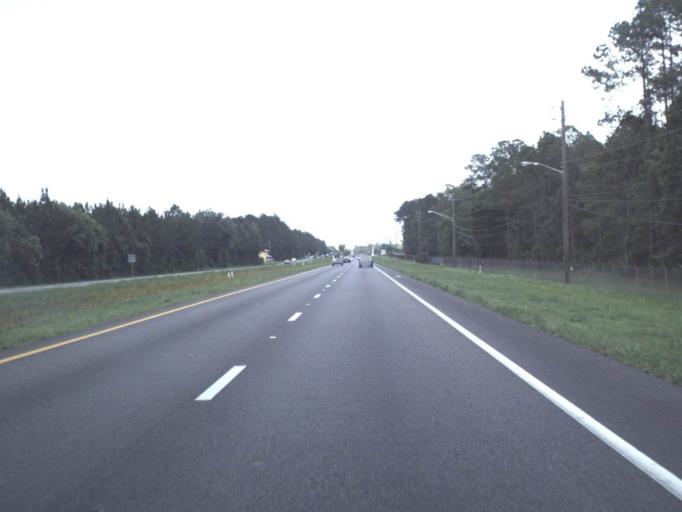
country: US
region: Florida
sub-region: Clay County
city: Bellair-Meadowbrook Terrace
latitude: 30.2804
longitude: -81.8175
